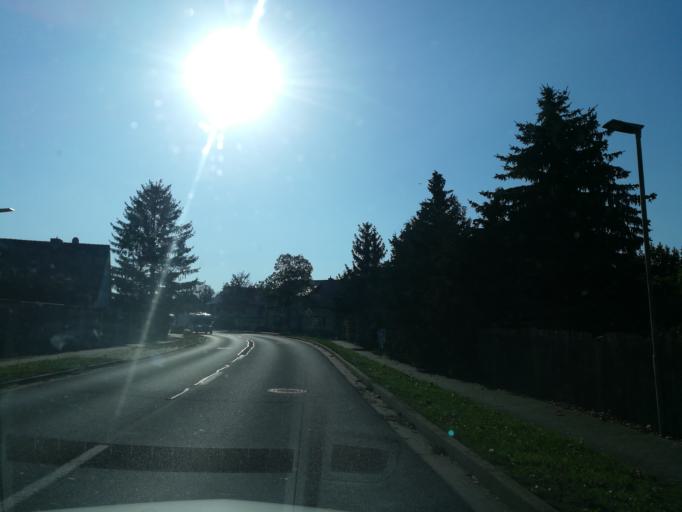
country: DE
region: Saxony-Anhalt
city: Wahlitz
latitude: 52.1174
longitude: 11.7653
